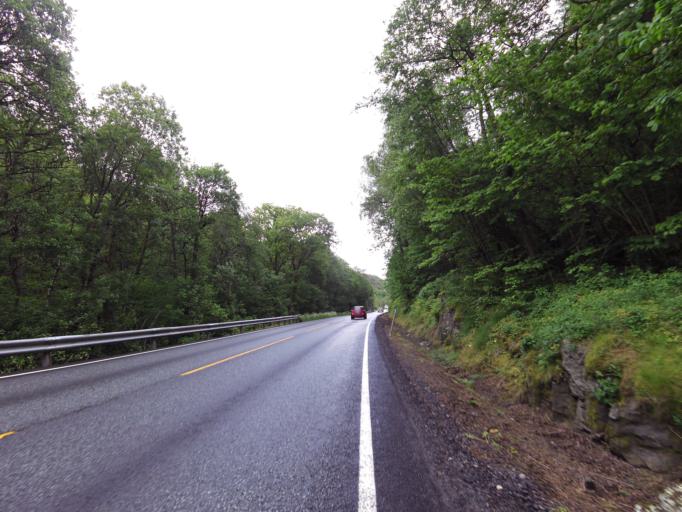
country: NO
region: Vest-Agder
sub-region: Farsund
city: Farsund
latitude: 58.1022
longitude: 6.8836
